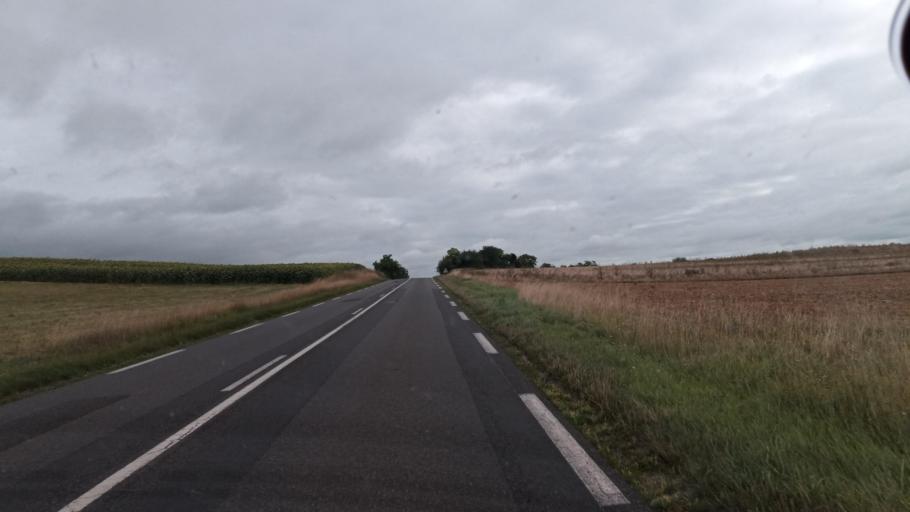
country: FR
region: Ile-de-France
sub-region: Departement de Seine-et-Marne
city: Cannes-Ecluse
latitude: 48.3309
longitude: 2.9568
